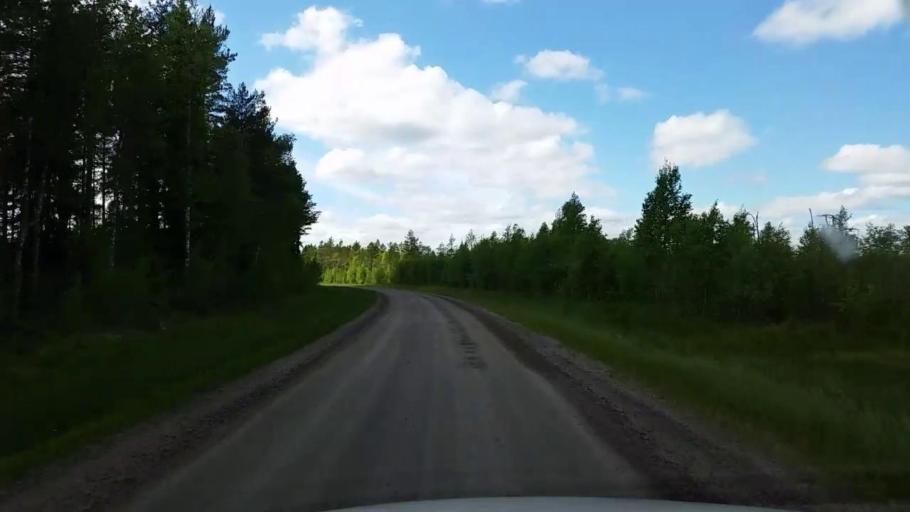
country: SE
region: Gaevleborg
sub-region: Ovanakers Kommun
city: Edsbyn
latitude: 61.5706
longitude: 15.9492
